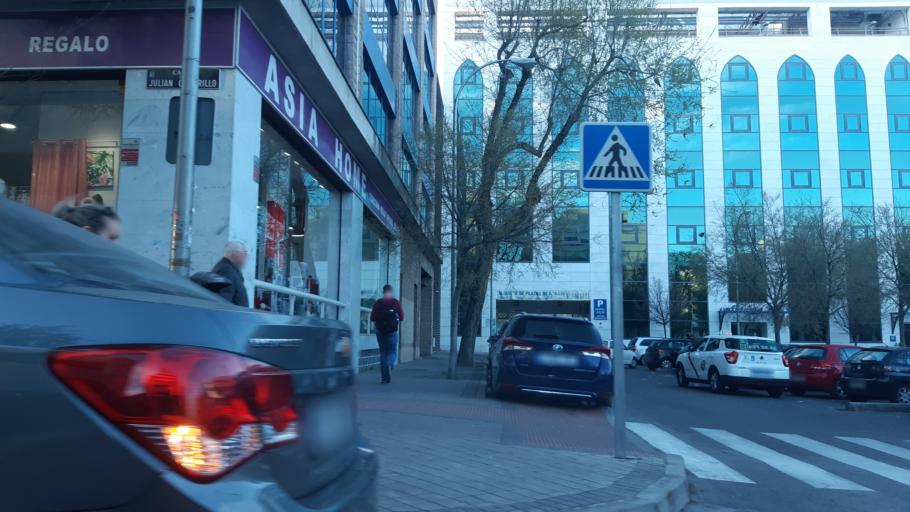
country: ES
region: Madrid
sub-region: Provincia de Madrid
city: San Blas
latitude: 40.4338
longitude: -3.6325
